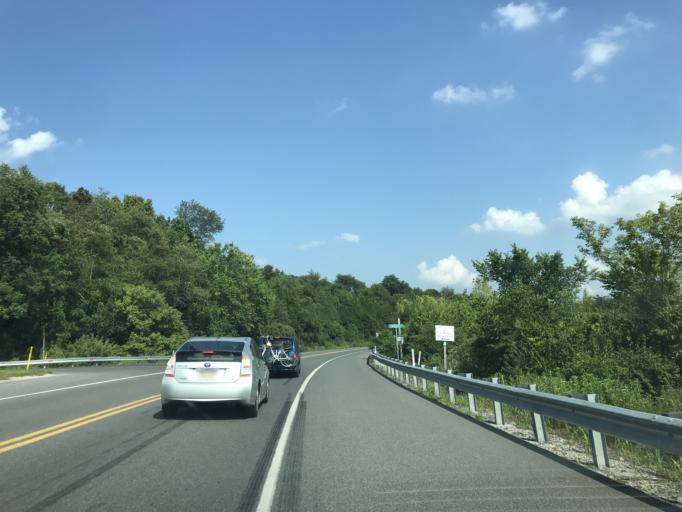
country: US
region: Pennsylvania
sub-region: York County
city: Parkville
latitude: 39.7816
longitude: -76.8860
